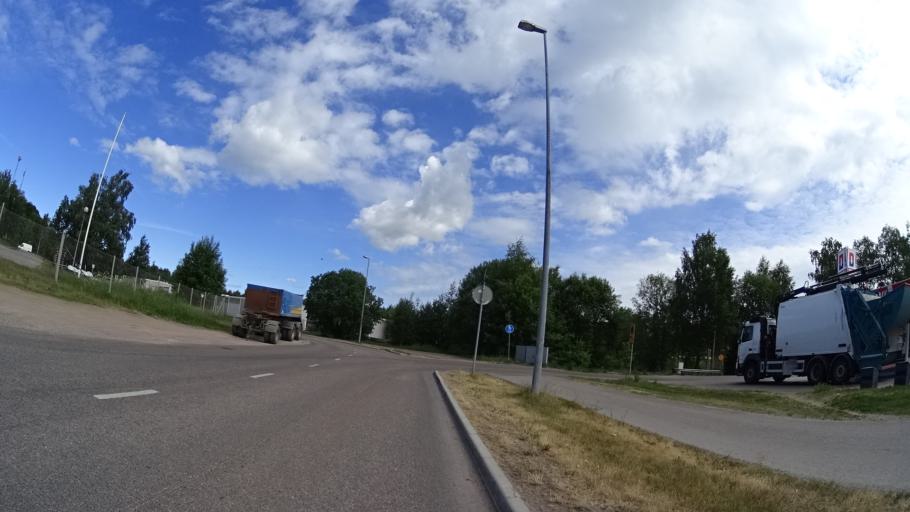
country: FI
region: Uusimaa
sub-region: Helsinki
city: Espoo
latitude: 60.2190
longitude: 24.6606
